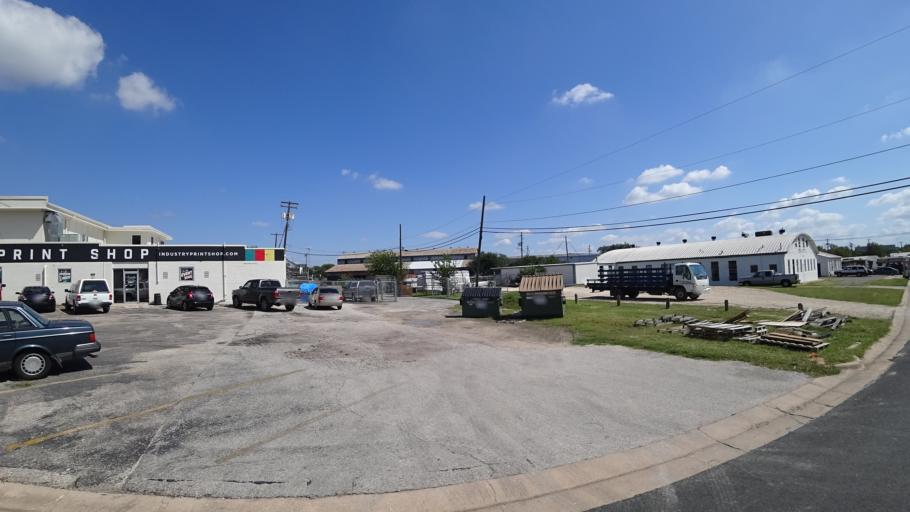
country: US
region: Texas
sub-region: Travis County
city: Austin
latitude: 30.3349
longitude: -97.7195
